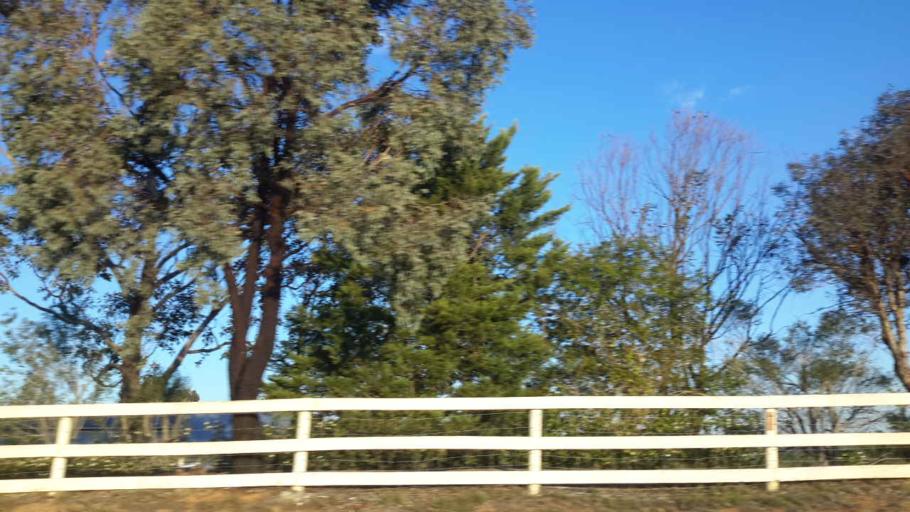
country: AU
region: New South Wales
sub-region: Wollondilly
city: Douglas Park
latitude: -34.1622
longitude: 150.7194
